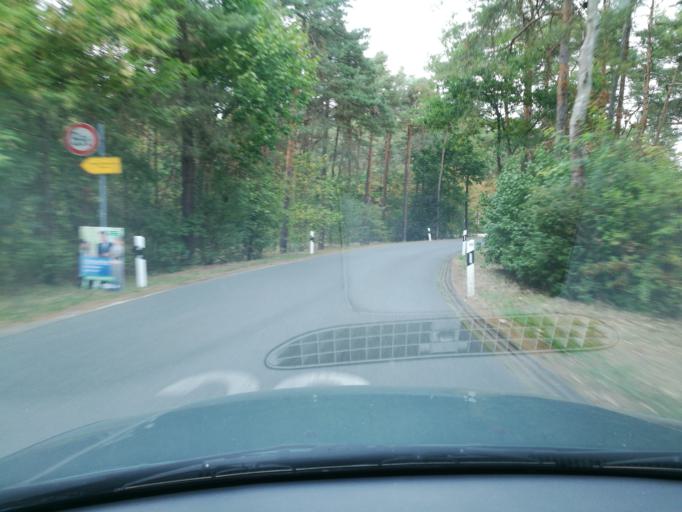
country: DE
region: Bavaria
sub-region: Regierungsbezirk Mittelfranken
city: Furth
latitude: 49.5063
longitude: 10.9851
